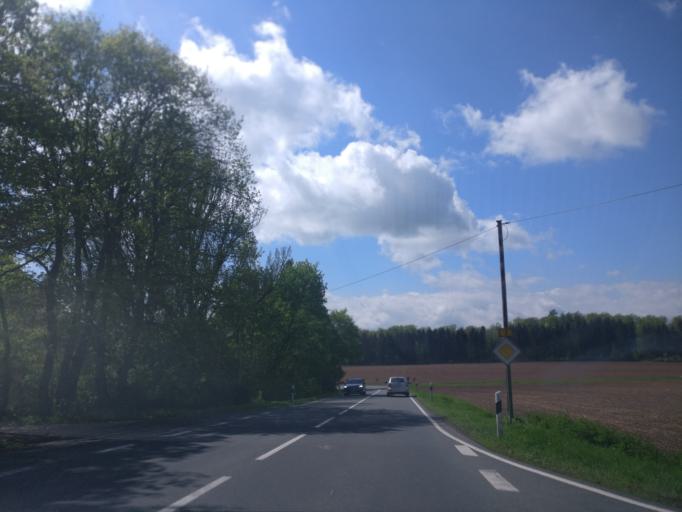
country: DE
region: Lower Saxony
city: Scheden
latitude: 51.4830
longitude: 9.7228
